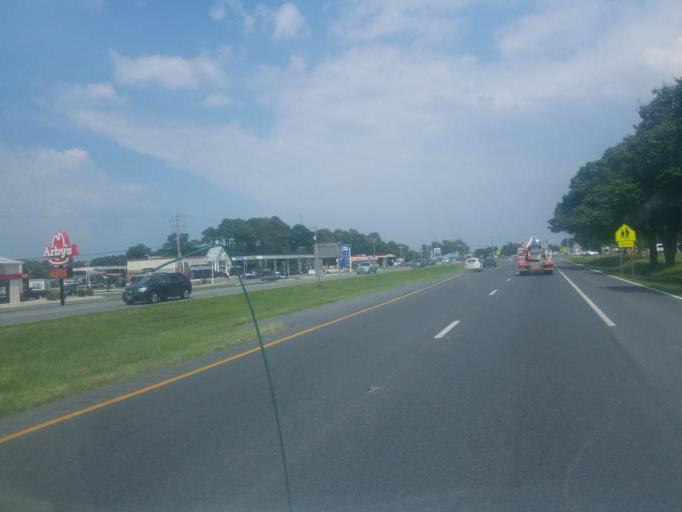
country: US
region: Maryland
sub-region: Worcester County
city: Berlin
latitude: 38.3425
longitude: -75.1921
